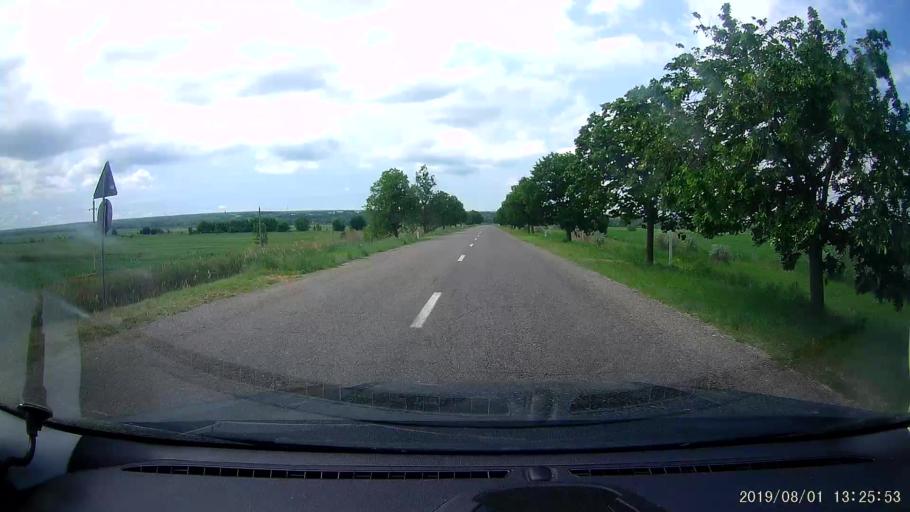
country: RO
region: Galati
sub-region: Comuna Oancea
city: Oancea
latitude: 45.9144
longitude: 28.1432
